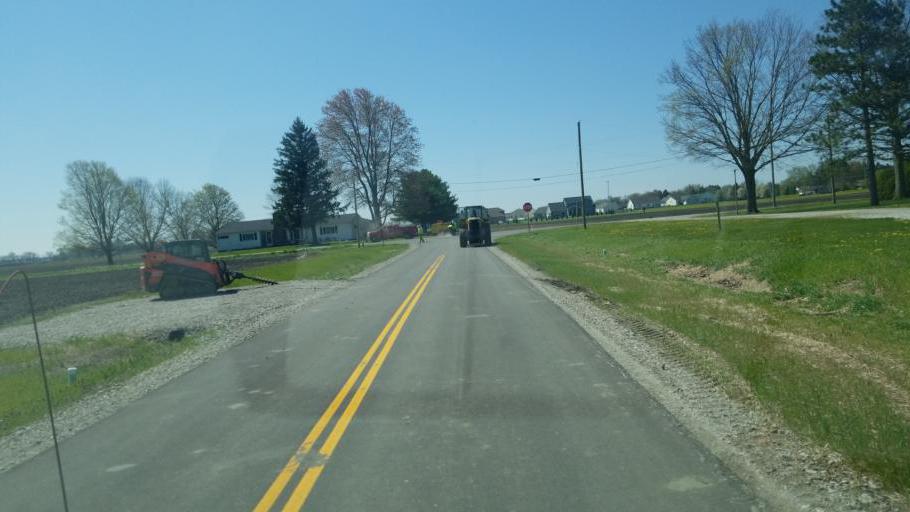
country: US
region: Ohio
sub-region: Marion County
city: Marion
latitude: 40.5992
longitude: -83.0713
